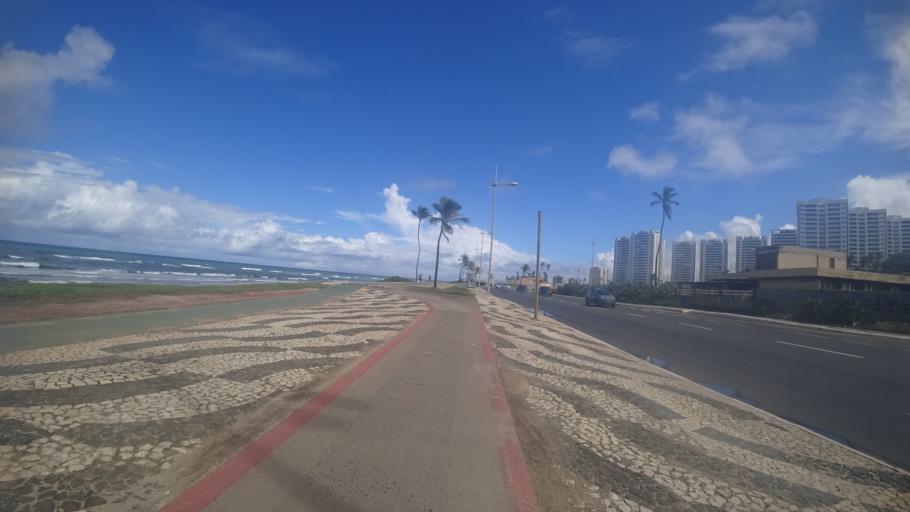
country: BR
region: Bahia
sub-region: Salvador
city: Salvador
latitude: -12.9672
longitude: -38.4054
